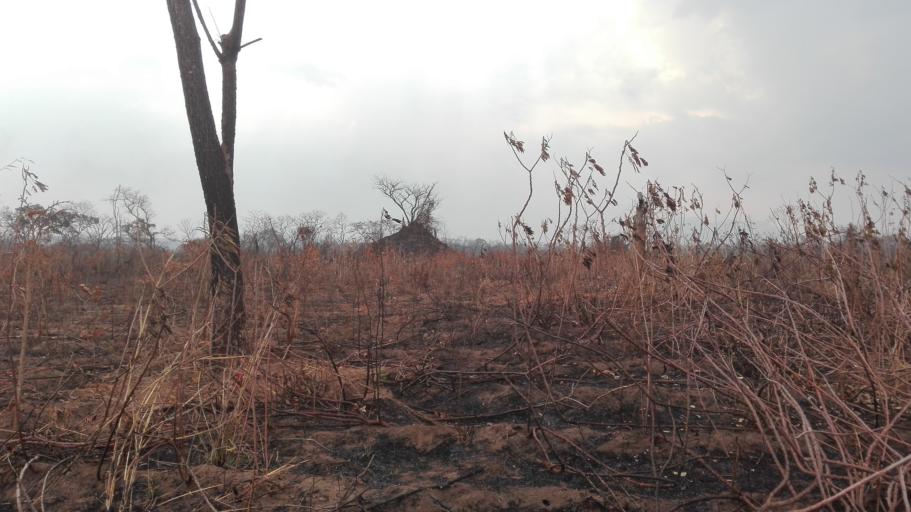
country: MZ
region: Nampula
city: Mutuali
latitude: -15.6485
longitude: 36.9255
